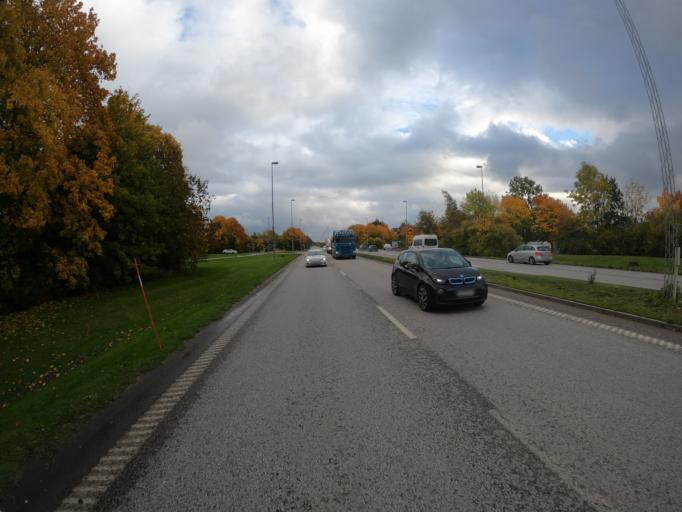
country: SE
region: Skane
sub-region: Lunds Kommun
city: Lund
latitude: 55.6974
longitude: 13.2220
